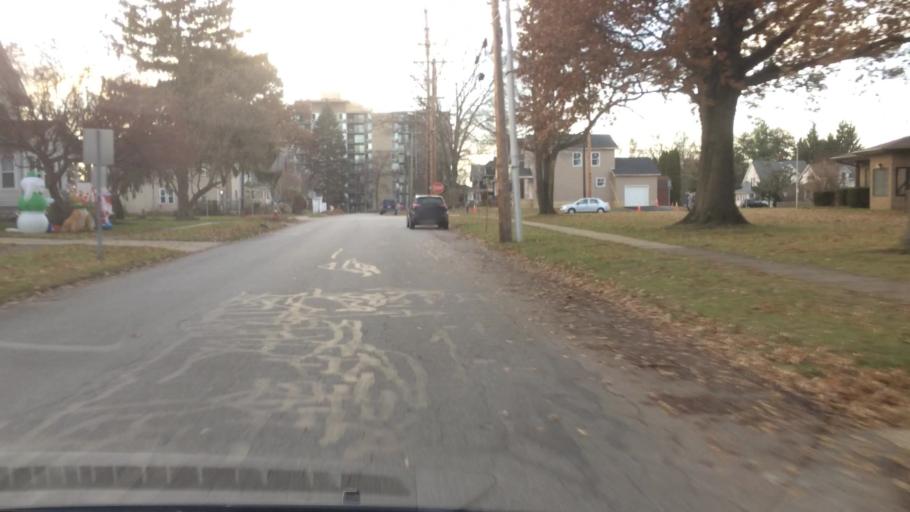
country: US
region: Ohio
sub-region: Summit County
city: Cuyahoga Falls
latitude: 41.1358
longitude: -81.4718
